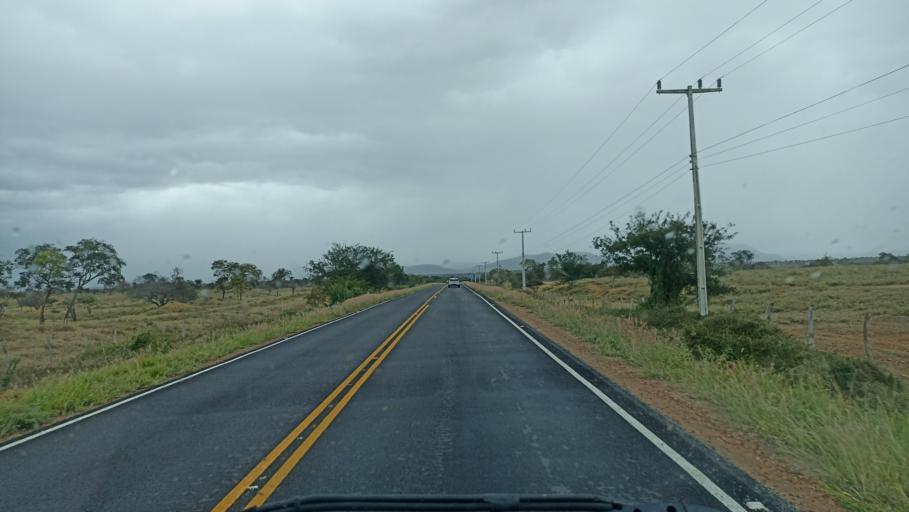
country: BR
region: Bahia
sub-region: Maracas
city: Maracas
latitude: -13.0368
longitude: -40.6944
